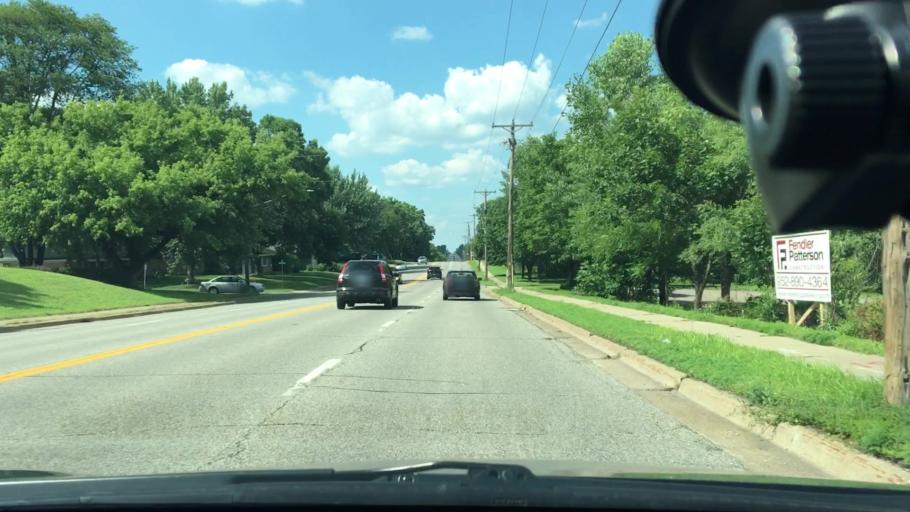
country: US
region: Minnesota
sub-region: Hennepin County
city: New Hope
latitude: 45.0153
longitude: -93.3802
